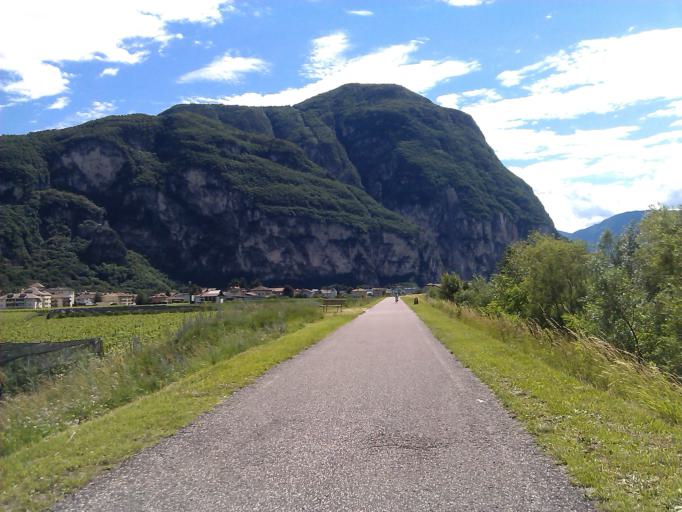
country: IT
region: Trentino-Alto Adige
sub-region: Bolzano
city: Salorno
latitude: 46.2475
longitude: 11.2118
